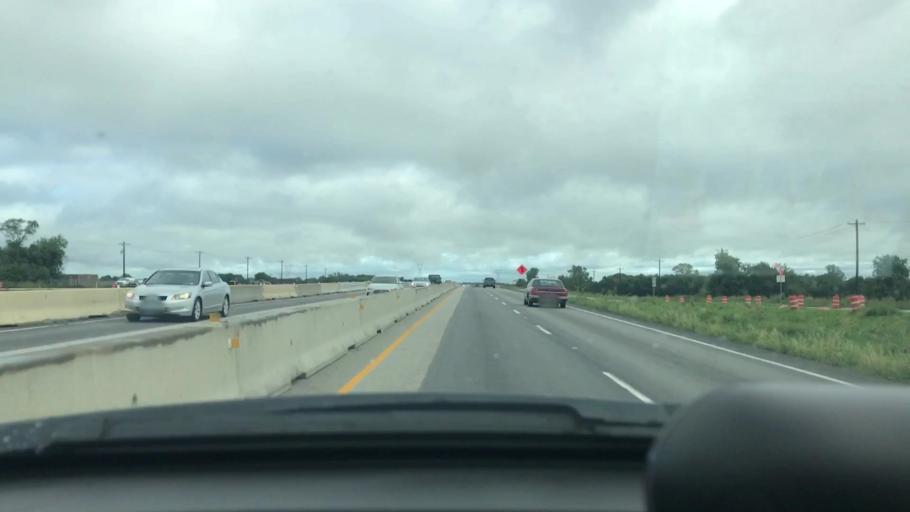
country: US
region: Texas
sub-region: Collin County
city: Anna
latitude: 33.3551
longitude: -96.5846
